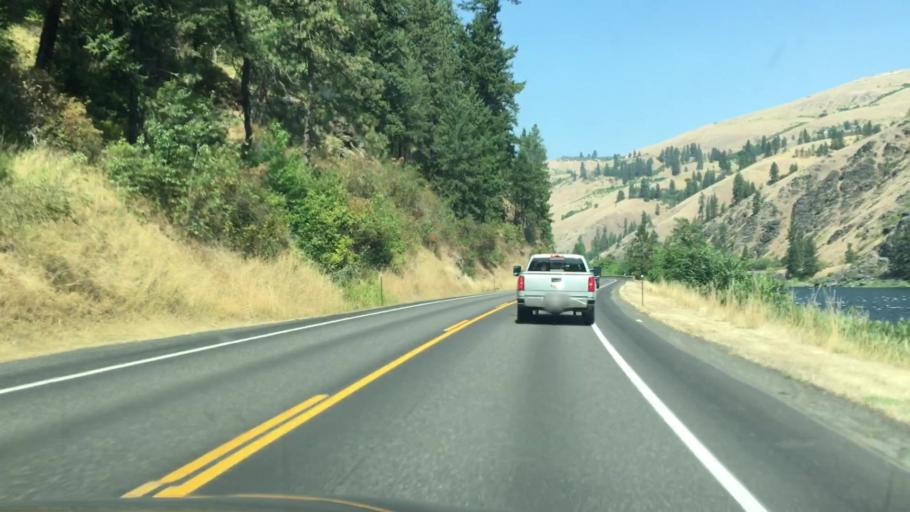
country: US
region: Idaho
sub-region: Clearwater County
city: Orofino
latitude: 46.4920
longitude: -116.4592
